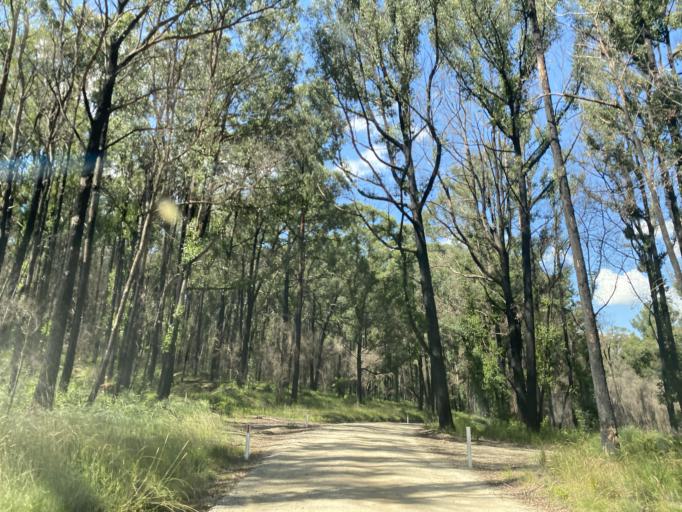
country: AU
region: Victoria
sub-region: Cardinia
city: Gembrook
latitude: -37.9812
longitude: 145.6305
